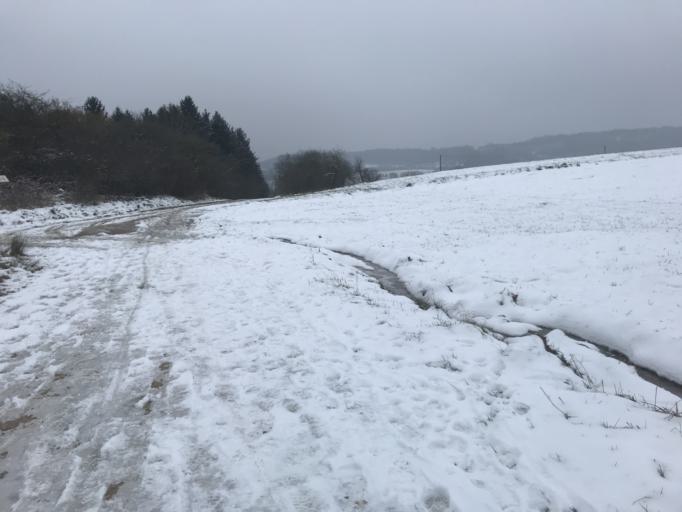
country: FR
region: Lorraine
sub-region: Departement de la Moselle
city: Russange
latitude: 49.4966
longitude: 5.9400
